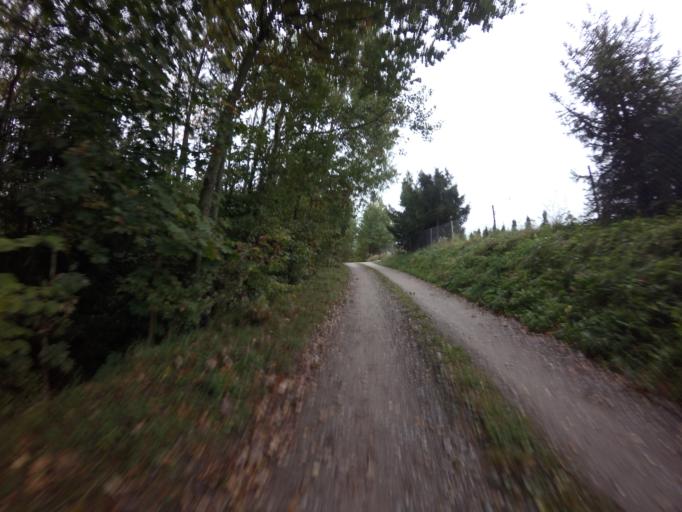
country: PL
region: Pomeranian Voivodeship
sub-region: Powiat kartuski
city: Stezyca
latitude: 54.1709
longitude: 17.9584
